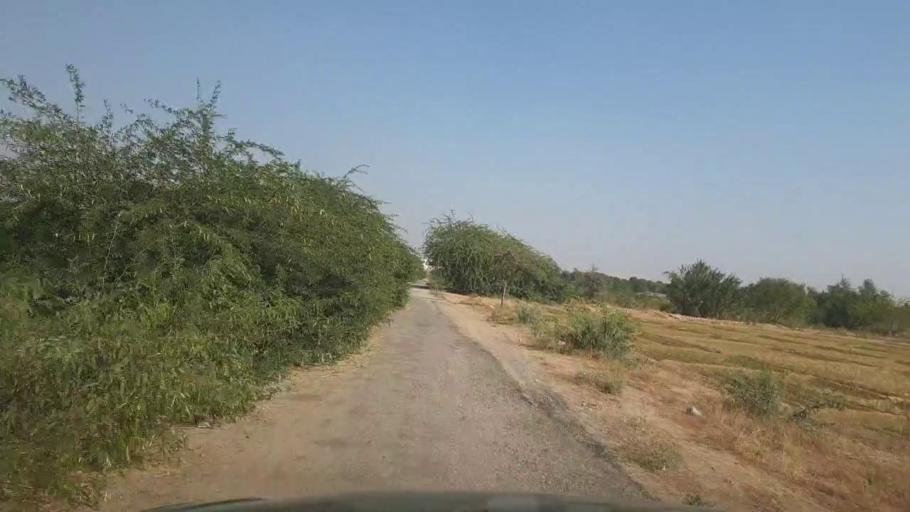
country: PK
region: Sindh
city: Jamshoro
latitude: 25.4080
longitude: 67.7776
